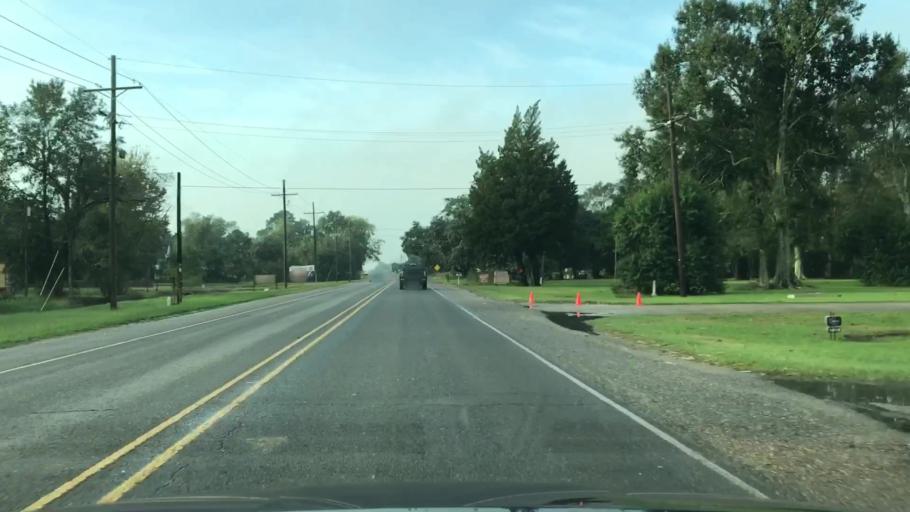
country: US
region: Louisiana
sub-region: Terrebonne Parish
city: Gray
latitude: 29.6746
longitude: -90.8145
